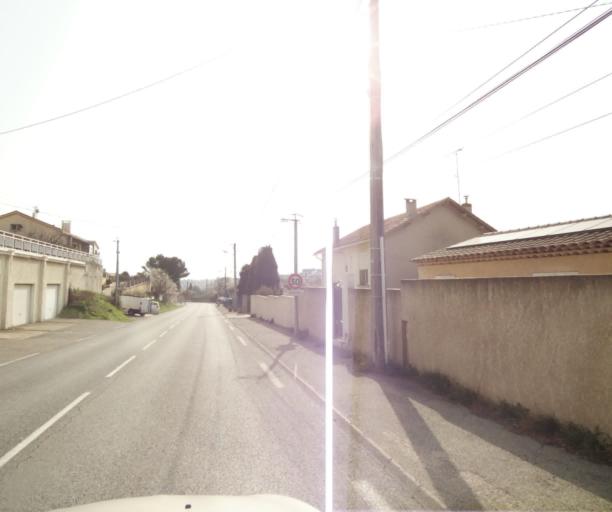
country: FR
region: Provence-Alpes-Cote d'Azur
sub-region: Departement des Bouches-du-Rhone
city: Marseille 15
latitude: 43.3924
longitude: 5.3439
